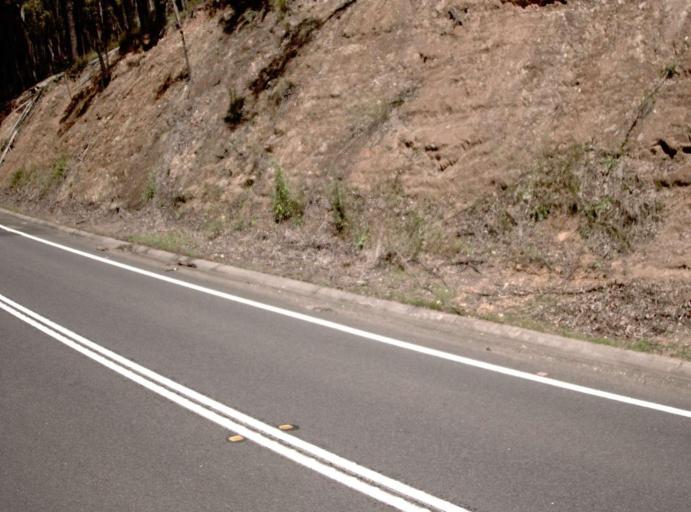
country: AU
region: New South Wales
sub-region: Bombala
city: Bombala
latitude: -37.5852
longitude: 148.9366
